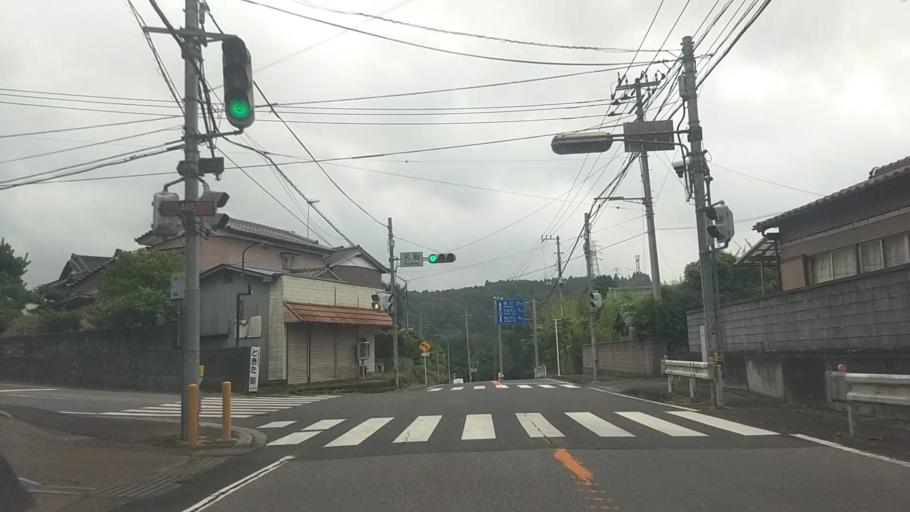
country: JP
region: Chiba
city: Kawaguchi
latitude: 35.2479
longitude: 140.0762
